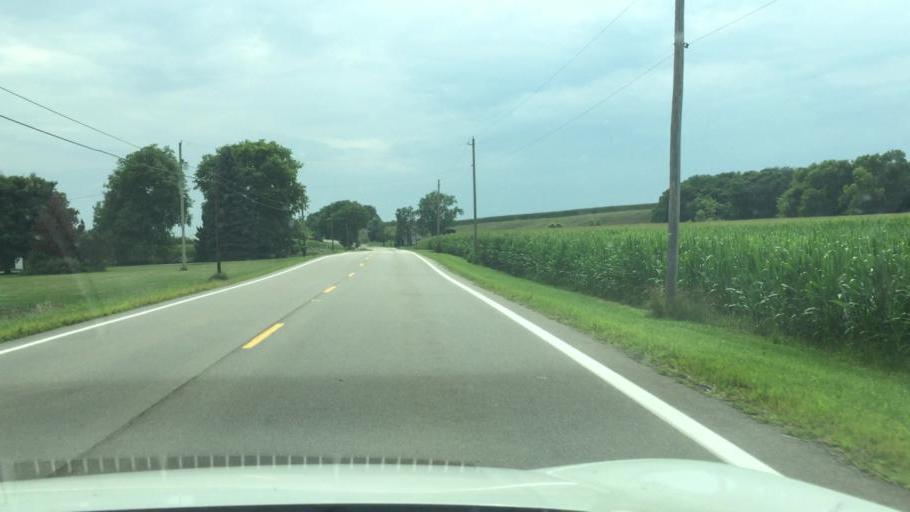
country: US
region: Ohio
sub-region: Clark County
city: Northridge
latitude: 40.0213
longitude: -83.6662
